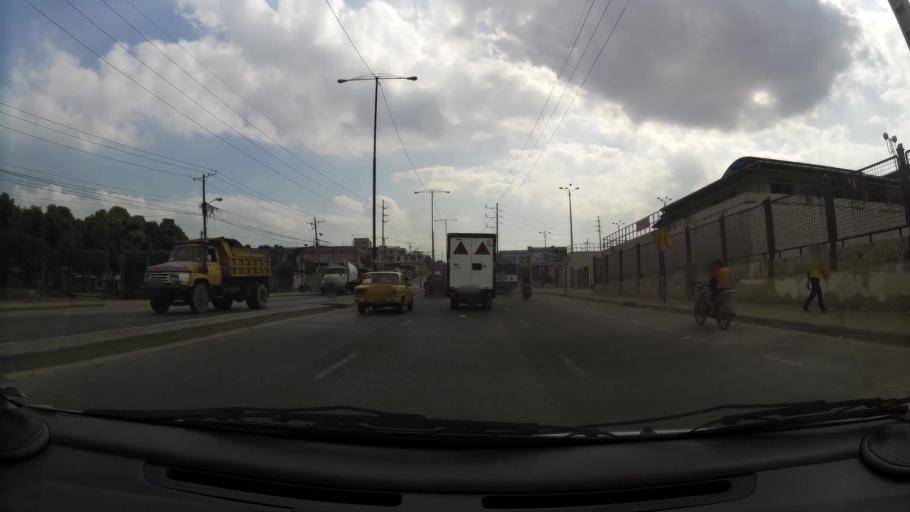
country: EC
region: Guayas
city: Santa Lucia
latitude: -2.1192
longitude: -79.9564
